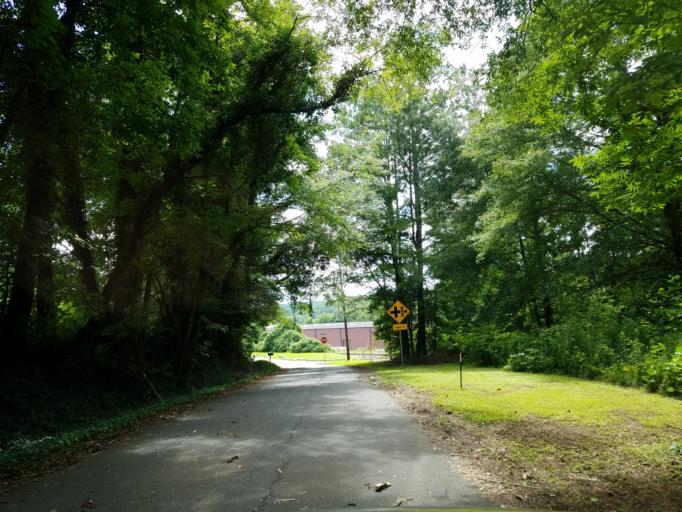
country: US
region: Georgia
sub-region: Cherokee County
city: Ball Ground
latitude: 34.3351
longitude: -84.3760
